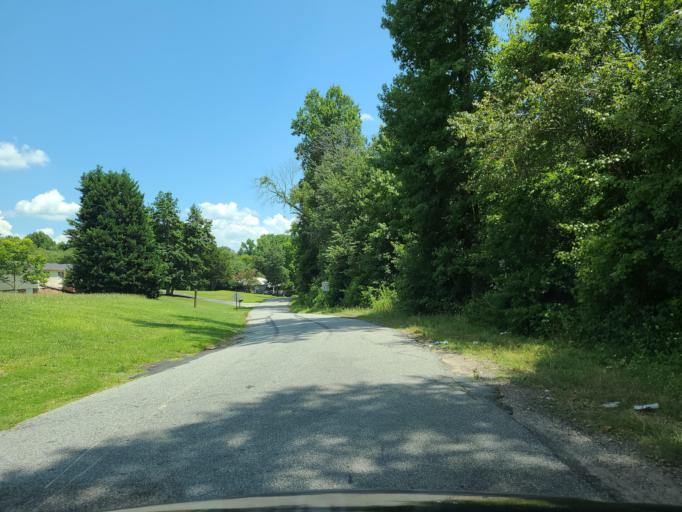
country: US
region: South Carolina
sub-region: Spartanburg County
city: Inman Mills
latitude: 35.0430
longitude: -82.1608
